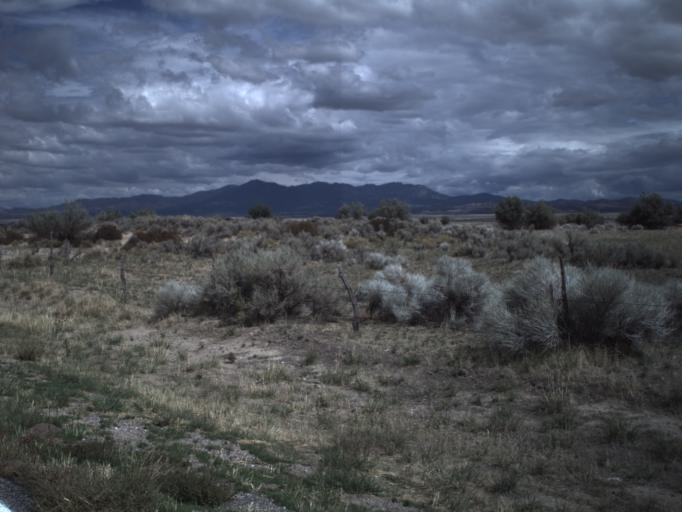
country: US
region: Utah
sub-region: Millard County
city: Fillmore
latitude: 39.0975
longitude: -112.4100
